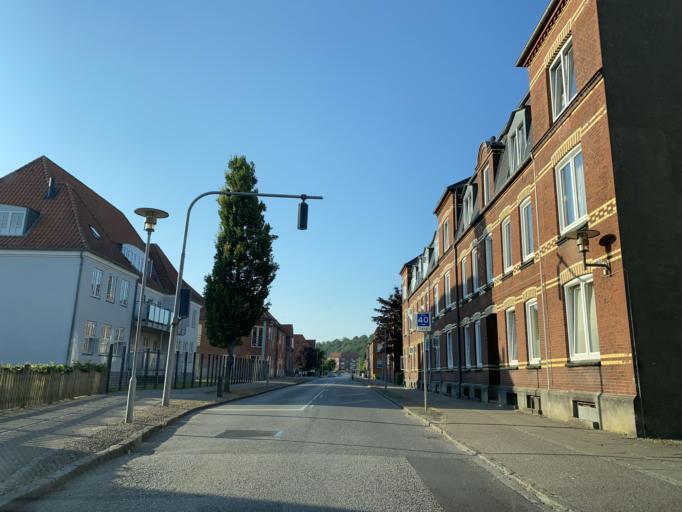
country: DK
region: South Denmark
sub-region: Aabenraa Kommune
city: Aabenraa
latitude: 55.0449
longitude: 9.4131
